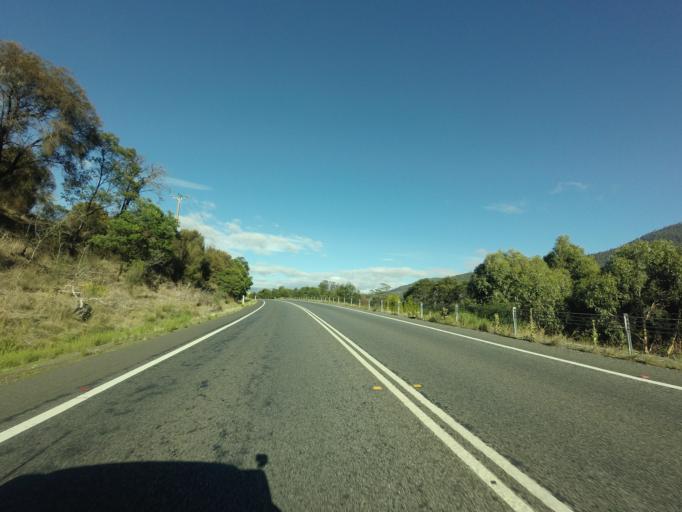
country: AU
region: Tasmania
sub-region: Glenorchy
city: Granton
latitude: -42.7581
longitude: 147.1505
